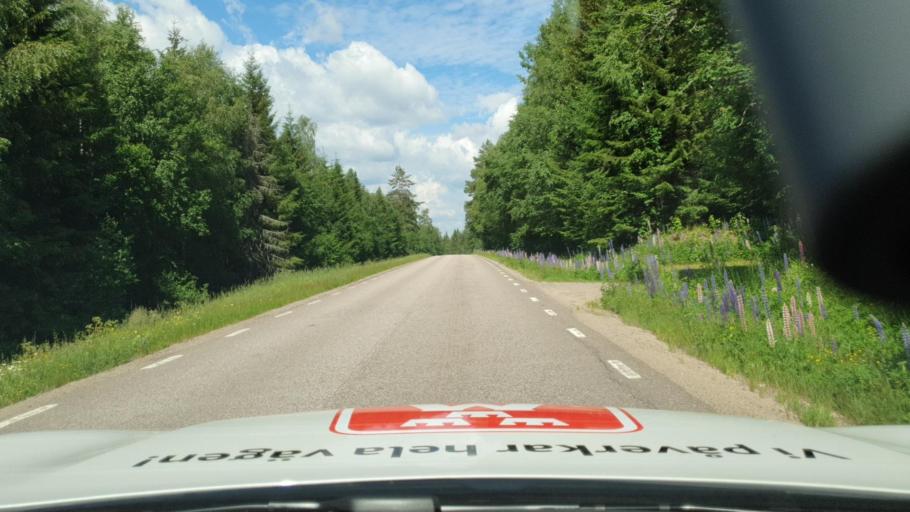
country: SE
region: Vaermland
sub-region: Torsby Kommun
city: Torsby
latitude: 60.4323
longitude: 12.9002
